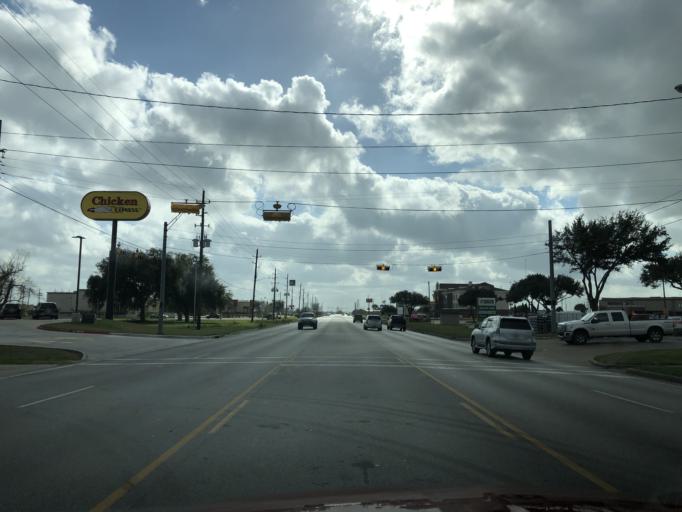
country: US
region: Texas
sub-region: Austin County
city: Sealy
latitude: 29.7620
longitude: -96.1517
